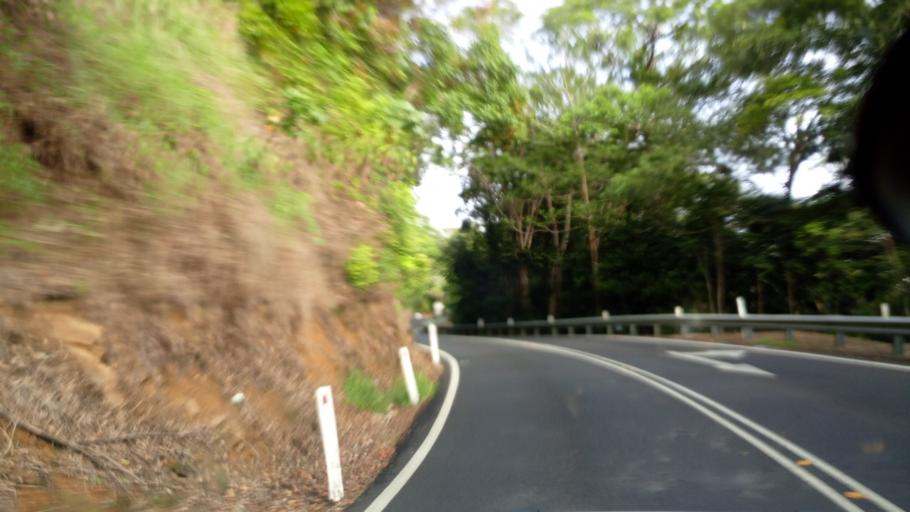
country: AU
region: Queensland
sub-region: Tablelands
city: Kuranda
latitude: -16.8371
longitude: 145.6715
